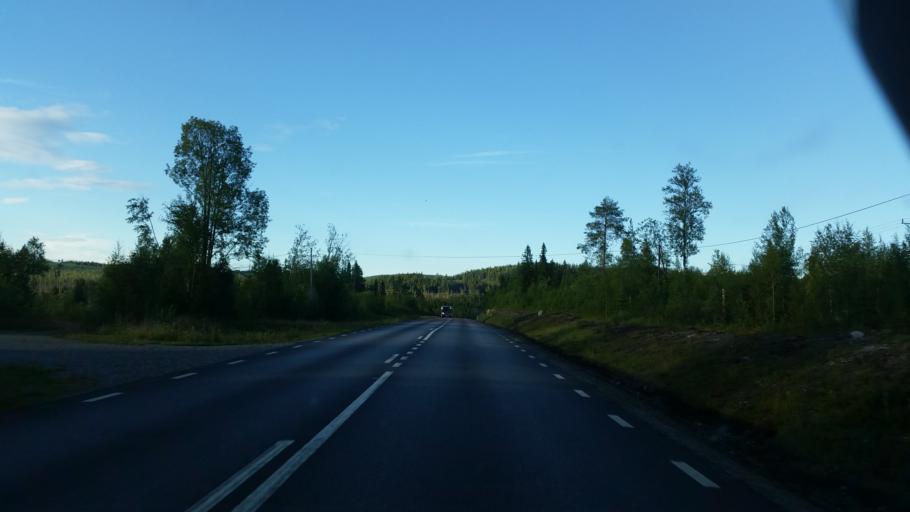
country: SE
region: Vaesterbotten
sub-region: Dorotea Kommun
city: Dorotea
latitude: 64.1791
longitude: 16.2981
